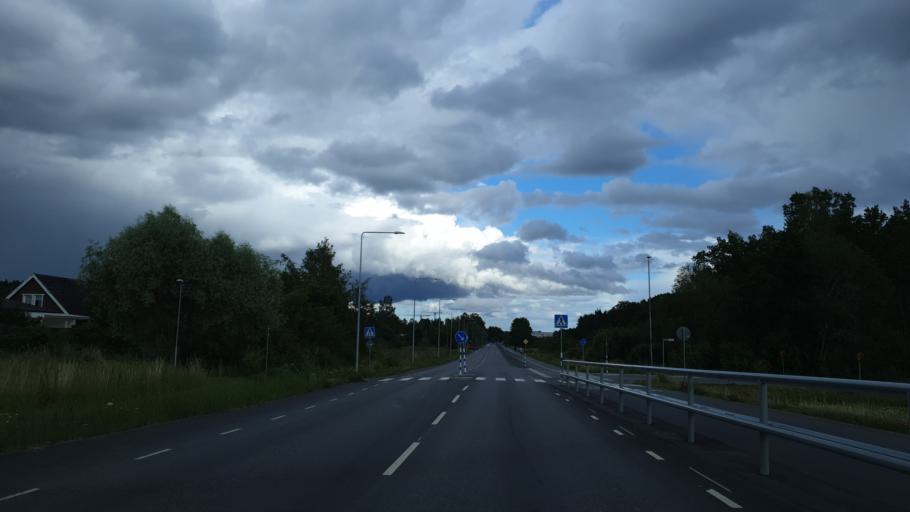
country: SE
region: Stockholm
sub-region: Jarfalla Kommun
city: Jakobsberg
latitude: 59.4234
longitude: 17.8033
